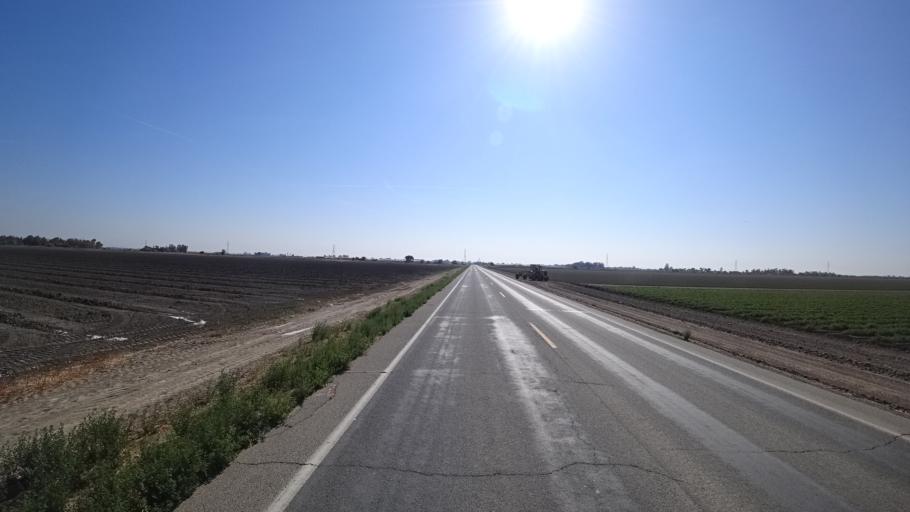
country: US
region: California
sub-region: Kings County
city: Lemoore Station
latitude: 36.3431
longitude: -119.9012
